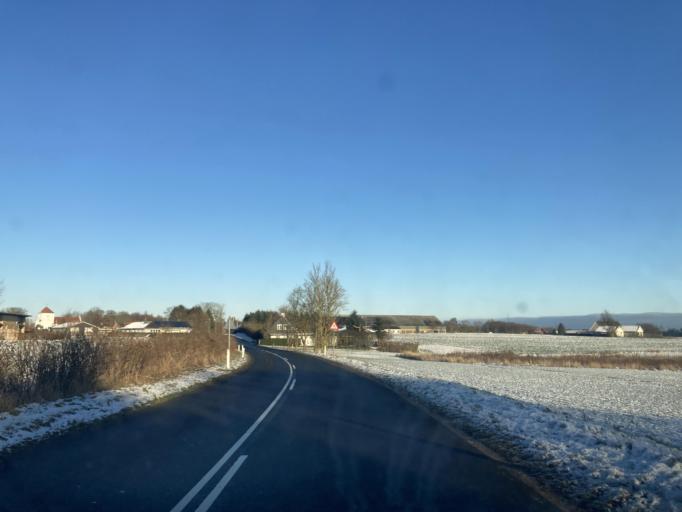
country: DK
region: South Denmark
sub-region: Svendborg Kommune
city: Thuro By
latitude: 55.1461
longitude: 10.7059
